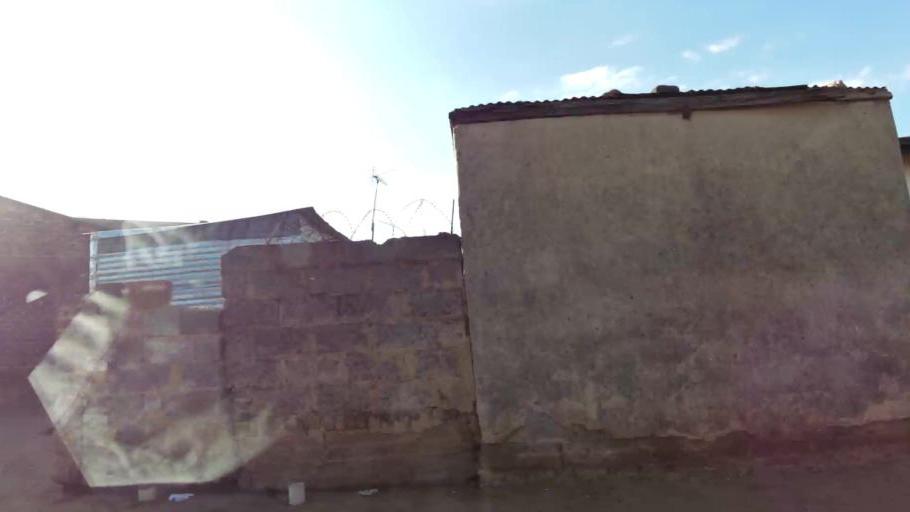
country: ZA
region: Gauteng
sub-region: City of Johannesburg Metropolitan Municipality
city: Roodepoort
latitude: -26.2164
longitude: 27.8768
